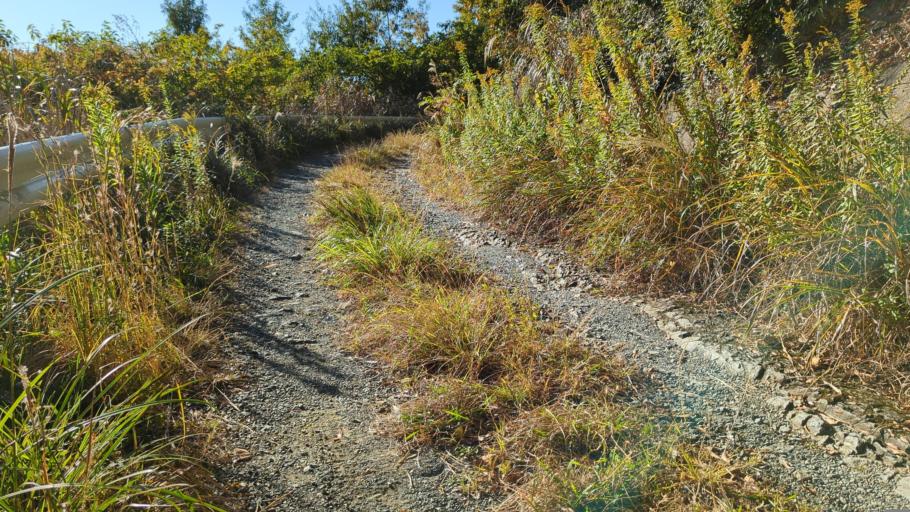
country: JP
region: Aichi
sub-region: Tokai-shi
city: Toyokawa
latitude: 34.7876
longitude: 137.4677
